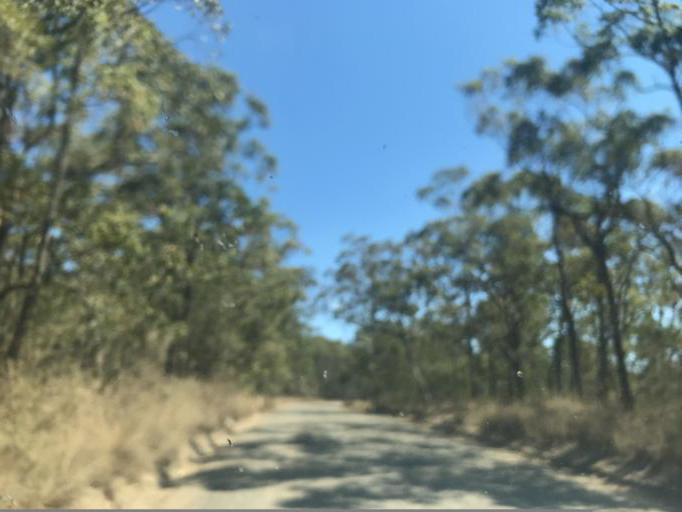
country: AU
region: New South Wales
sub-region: Hawkesbury
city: Pitt Town
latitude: -33.4636
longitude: 150.8342
